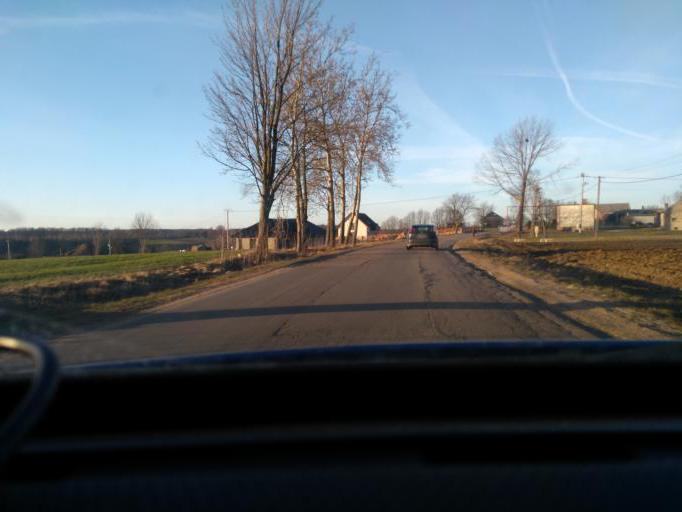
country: PL
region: Pomeranian Voivodeship
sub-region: Powiat kartuski
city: Przodkowo
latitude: 54.3942
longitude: 18.2889
